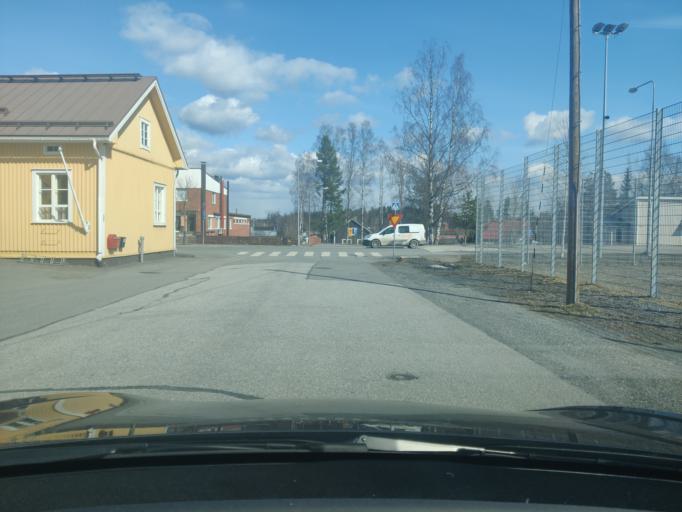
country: FI
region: Northern Savo
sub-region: Kuopio
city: Vehmersalmi
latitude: 62.9133
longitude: 28.1625
